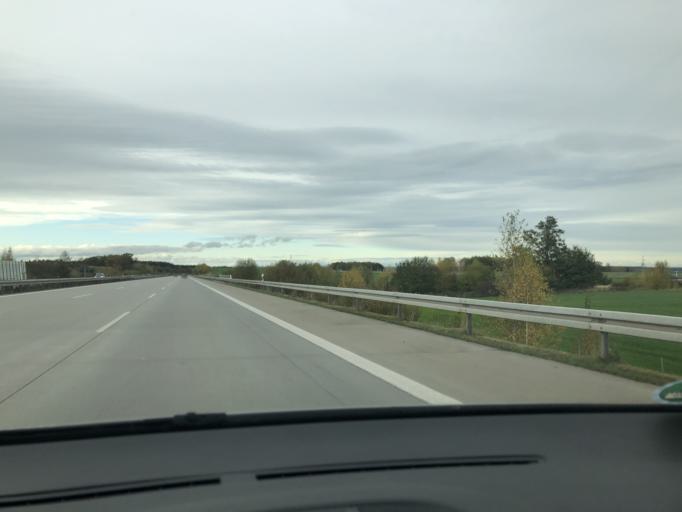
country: DE
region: Saxony
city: Callenberg
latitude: 50.8258
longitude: 12.6223
